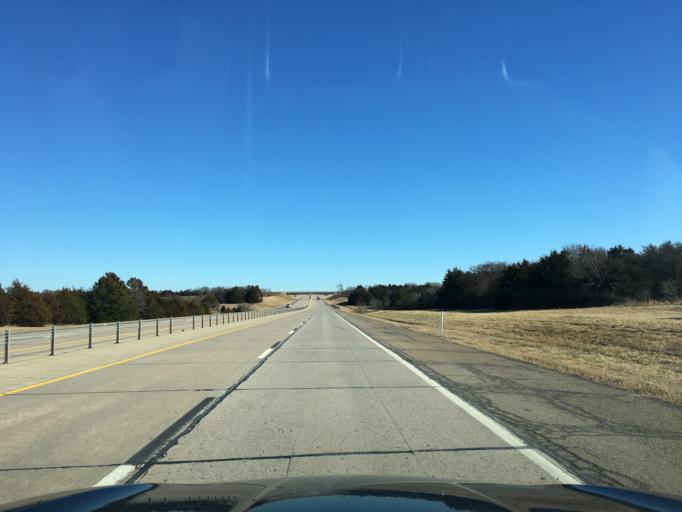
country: US
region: Oklahoma
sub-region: Pawnee County
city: Pawnee
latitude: 36.2247
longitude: -96.8256
